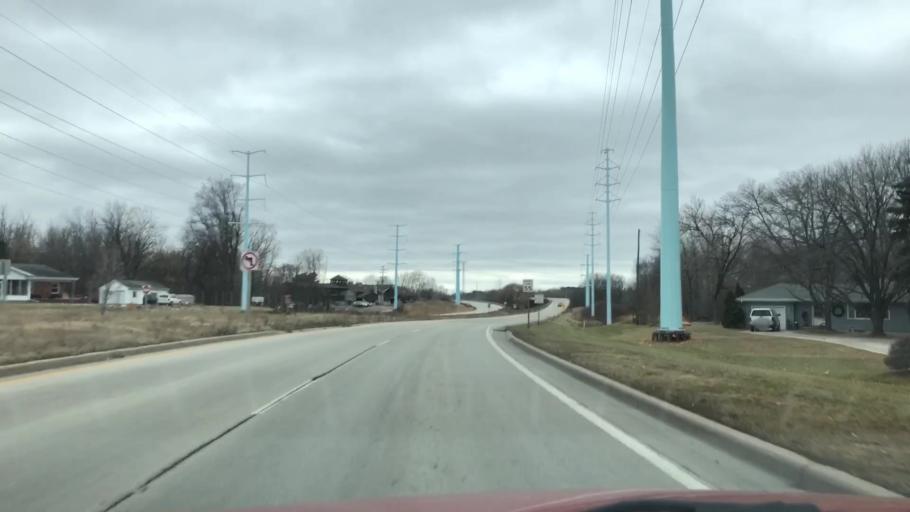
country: US
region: Wisconsin
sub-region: Brown County
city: De Pere
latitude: 44.4563
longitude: -88.0793
